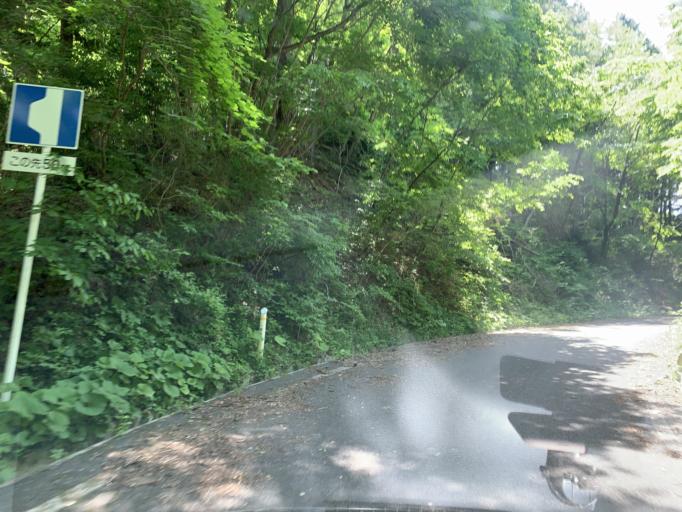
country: JP
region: Iwate
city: Ichinoseki
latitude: 38.9588
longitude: 141.2426
